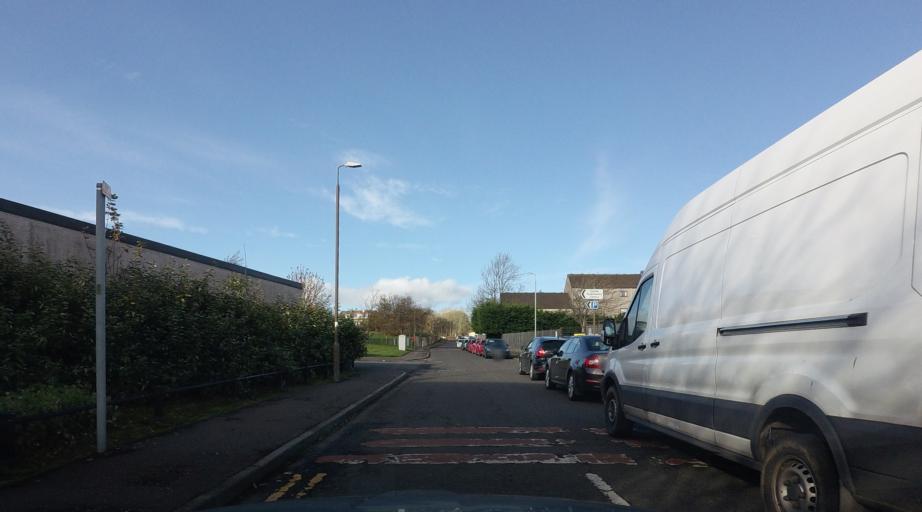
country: GB
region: Scotland
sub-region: West Lothian
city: Livingston
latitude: 55.9292
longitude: -3.5097
